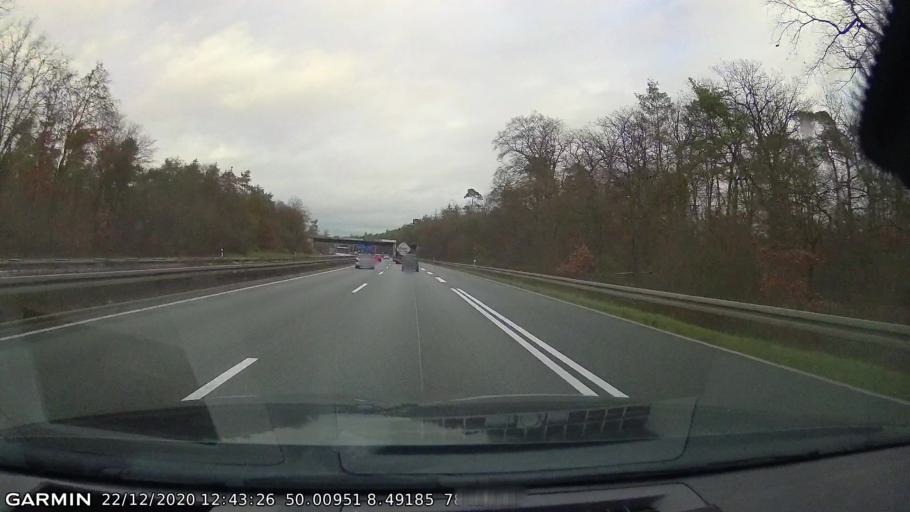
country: DE
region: Hesse
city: Raunheim
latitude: 50.0095
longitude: 8.4920
